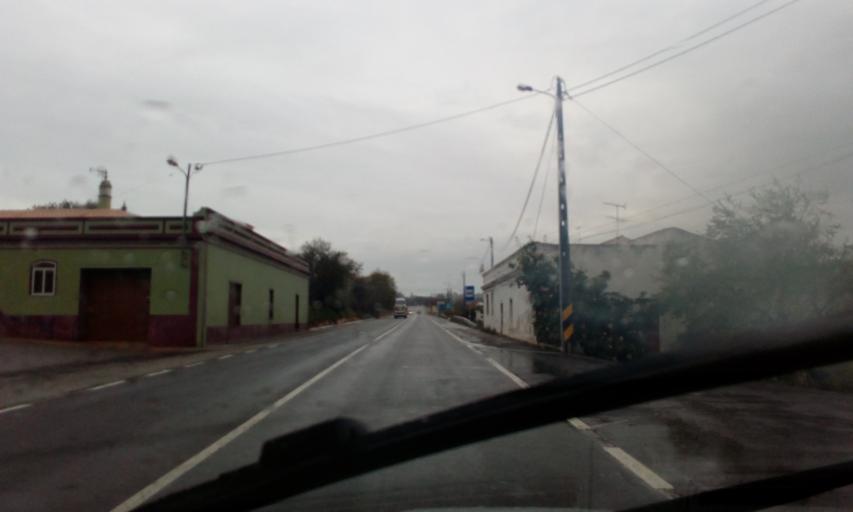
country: PT
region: Faro
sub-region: Silves
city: Armacao de Pera
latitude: 37.1349
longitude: -8.3782
